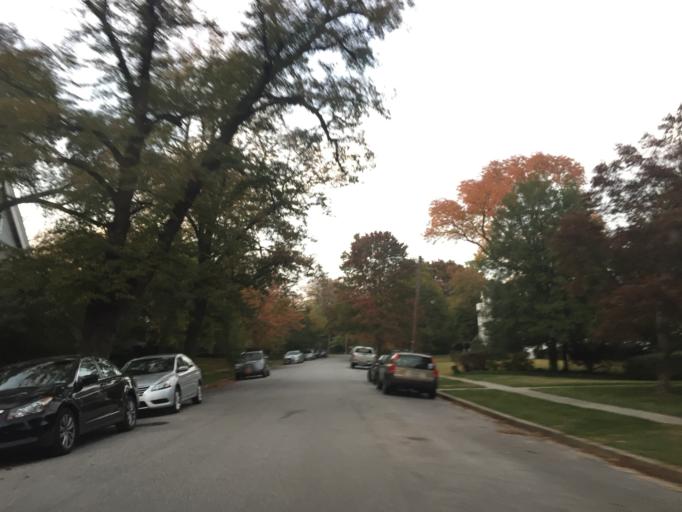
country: US
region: Maryland
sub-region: City of Baltimore
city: Baltimore
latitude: 39.3465
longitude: -76.6341
